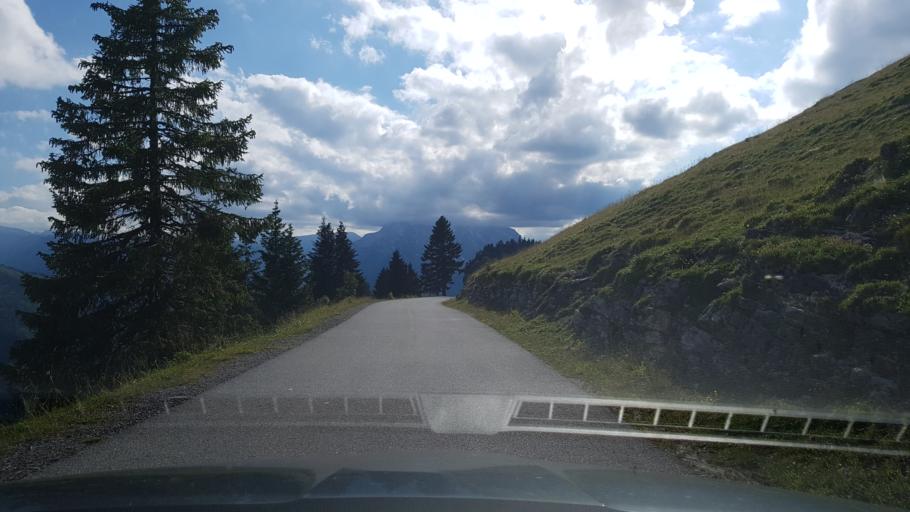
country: AT
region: Salzburg
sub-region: Politischer Bezirk Salzburg-Umgebung
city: Hintersee
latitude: 47.6359
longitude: 13.2683
